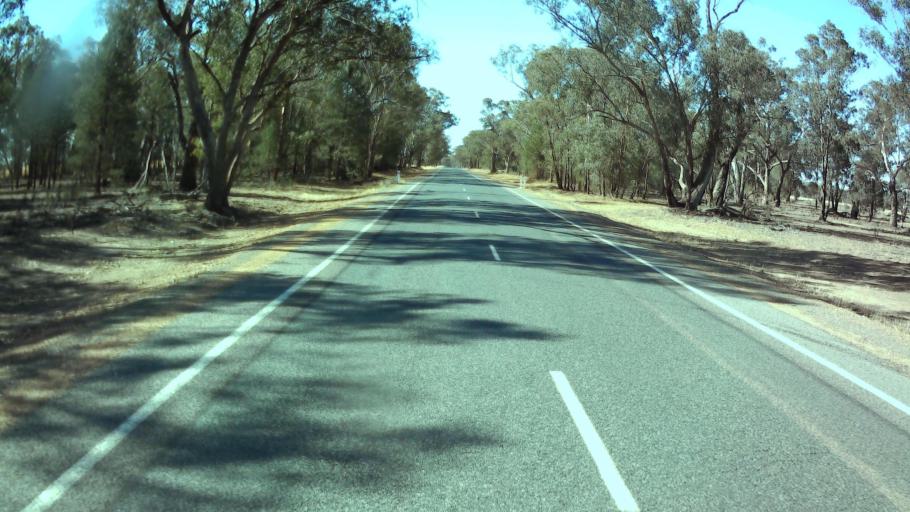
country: AU
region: New South Wales
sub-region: Weddin
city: Grenfell
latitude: -33.7424
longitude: 148.0887
